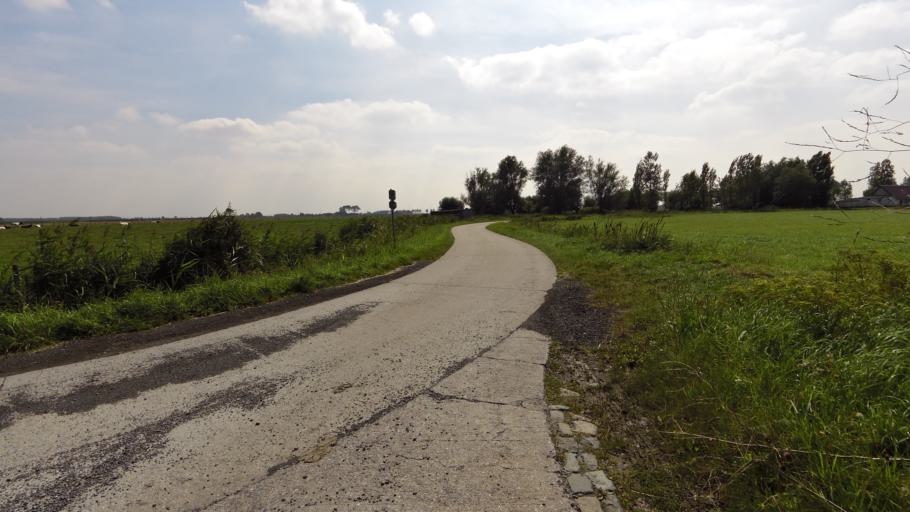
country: BE
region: Flanders
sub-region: Provincie West-Vlaanderen
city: Middelkerke
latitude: 51.1530
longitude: 2.8678
